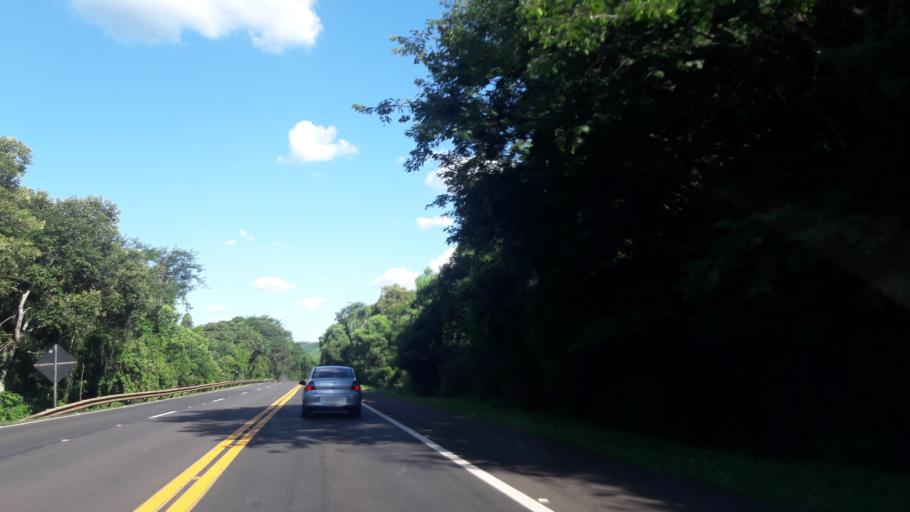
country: BR
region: Parana
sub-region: Laranjeiras Do Sul
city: Laranjeiras do Sul
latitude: -25.4151
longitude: -52.0764
